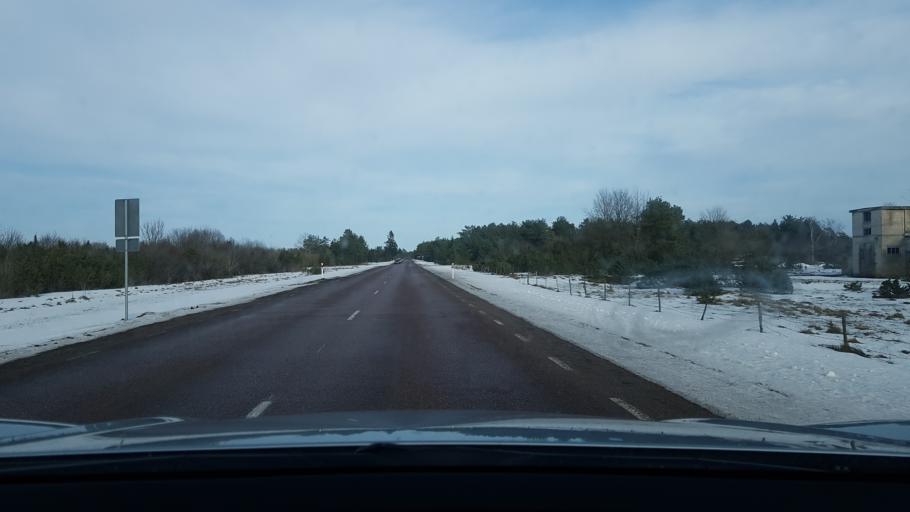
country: EE
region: Saare
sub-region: Kuressaare linn
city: Kuressaare
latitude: 58.3308
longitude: 22.5612
